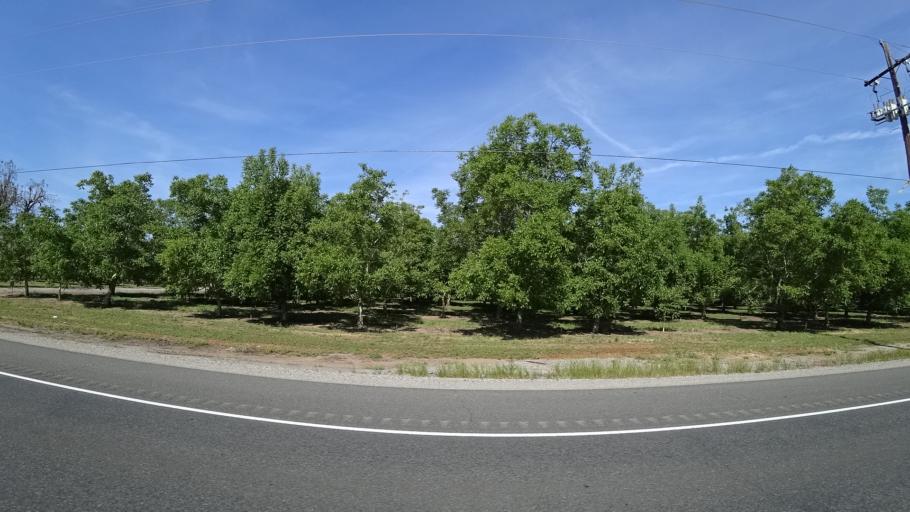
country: US
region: California
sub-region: Tehama County
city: Red Bluff
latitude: 40.1561
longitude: -122.1460
